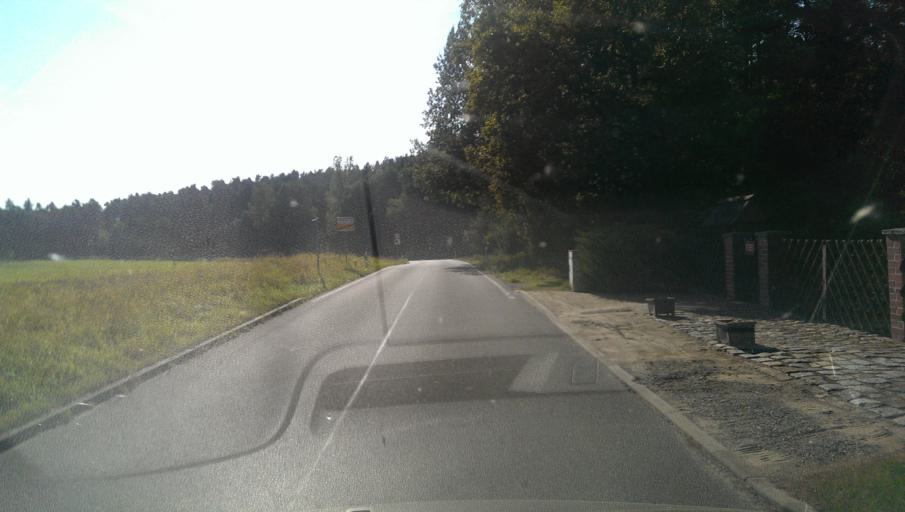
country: DE
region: Brandenburg
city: Halbe
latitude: 52.0700
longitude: 13.7223
